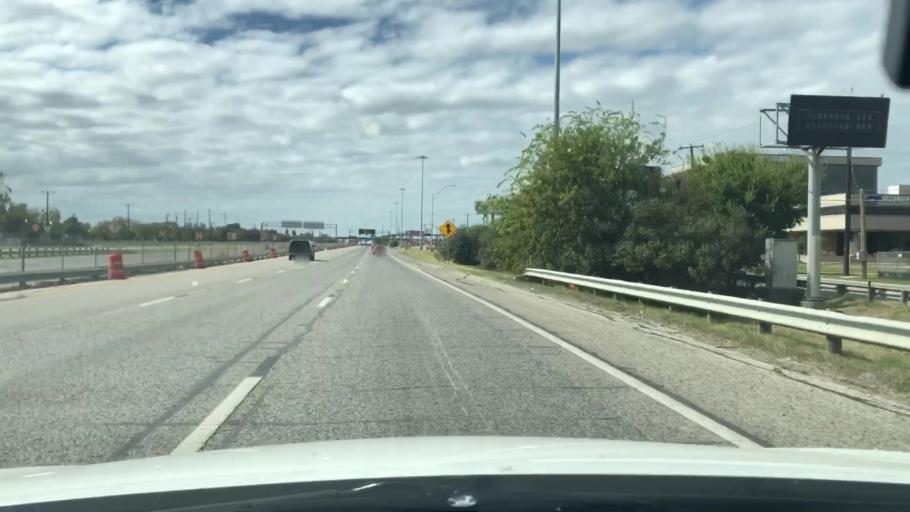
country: US
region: Texas
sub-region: Bexar County
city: Lackland Air Force Base
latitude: 29.4019
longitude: -98.6321
